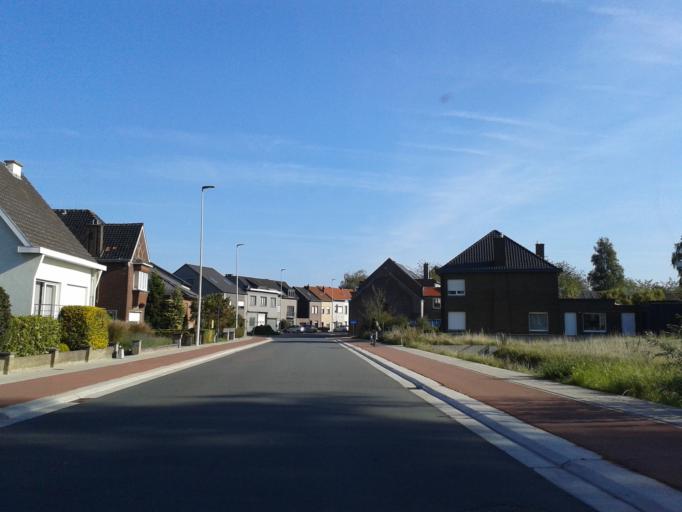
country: BE
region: Flanders
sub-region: Provincie Oost-Vlaanderen
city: Aalst
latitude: 50.9588
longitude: 4.0524
